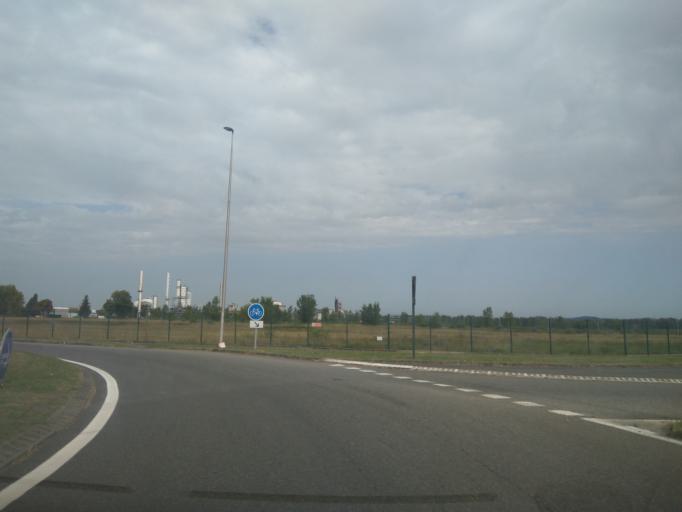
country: FR
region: Aquitaine
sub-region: Departement des Pyrenees-Atlantiques
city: Mourenx
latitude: 43.3647
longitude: -0.5771
